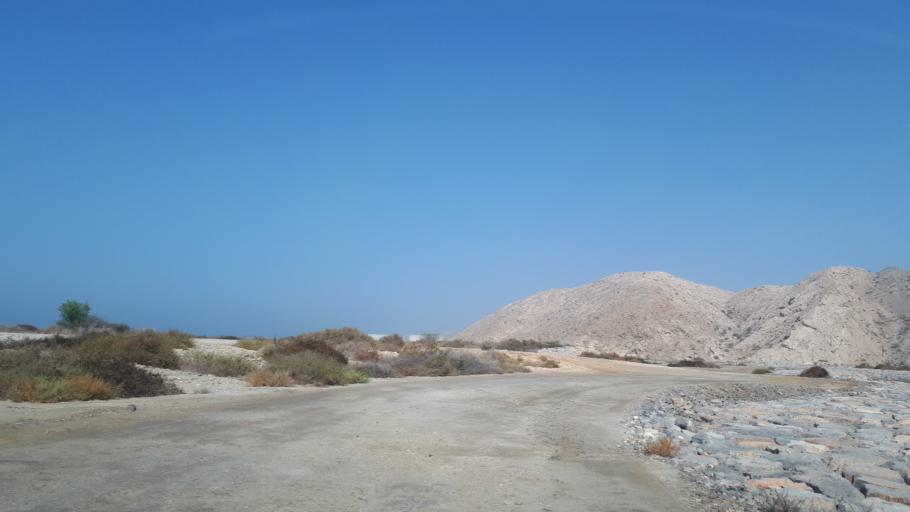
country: OM
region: Muhafazat Masqat
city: Muscat
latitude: 23.5387
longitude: 58.6627
